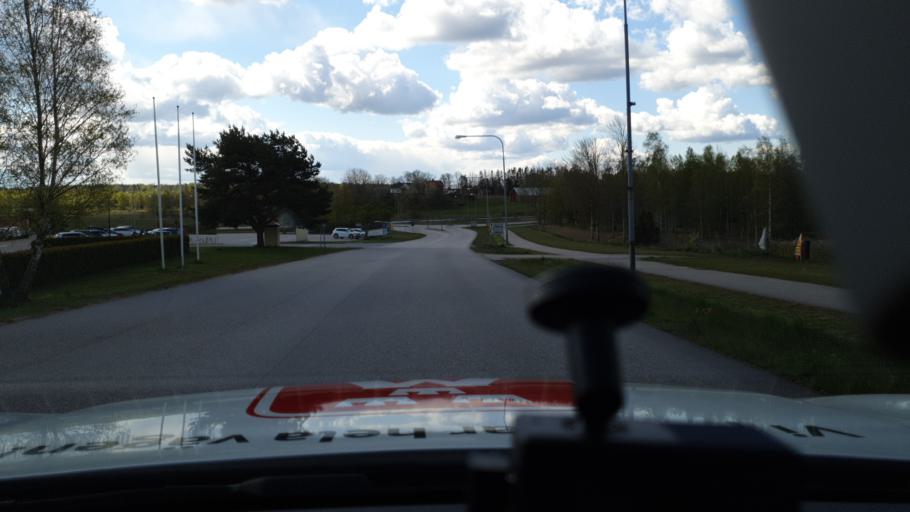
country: SE
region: Kalmar
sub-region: Vimmerby Kommun
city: Vimmerby
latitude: 57.6624
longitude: 15.8762
